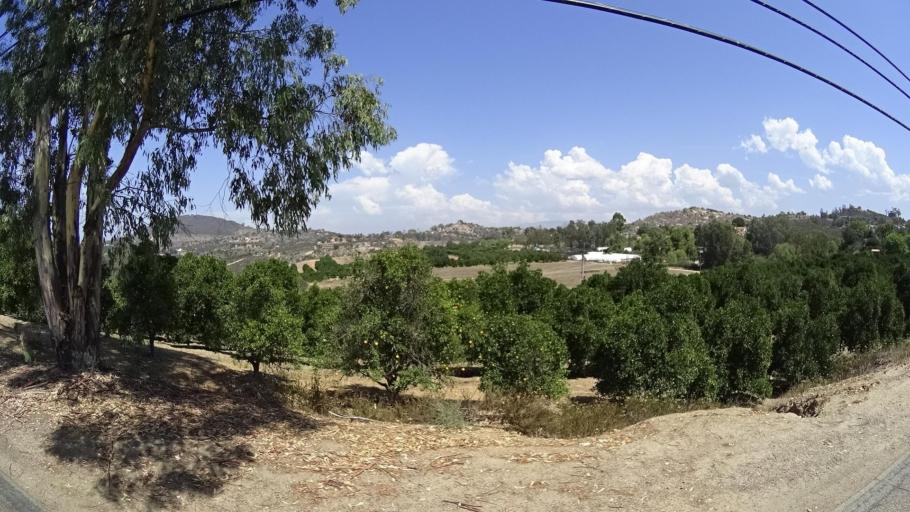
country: US
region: California
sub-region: San Diego County
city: Hidden Meadows
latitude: 33.2272
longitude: -117.0743
